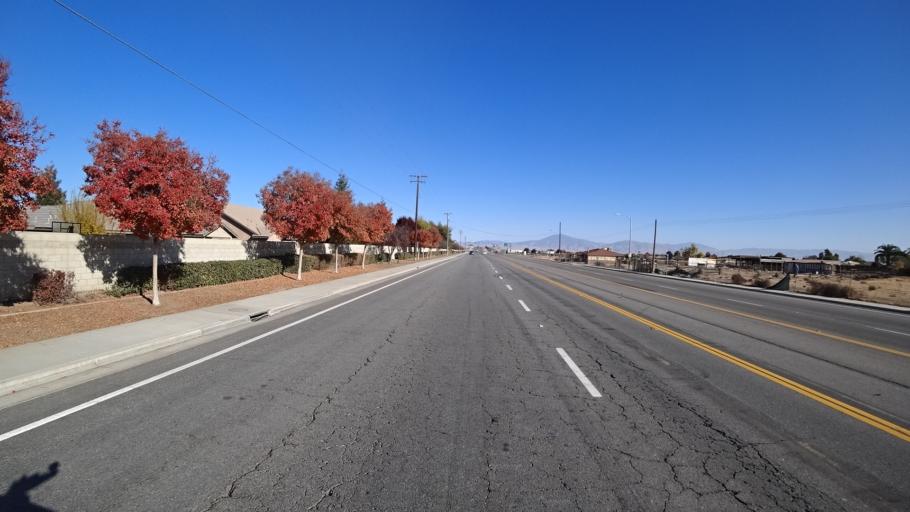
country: US
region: California
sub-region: Kern County
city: Greenfield
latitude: 35.2814
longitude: -119.0336
